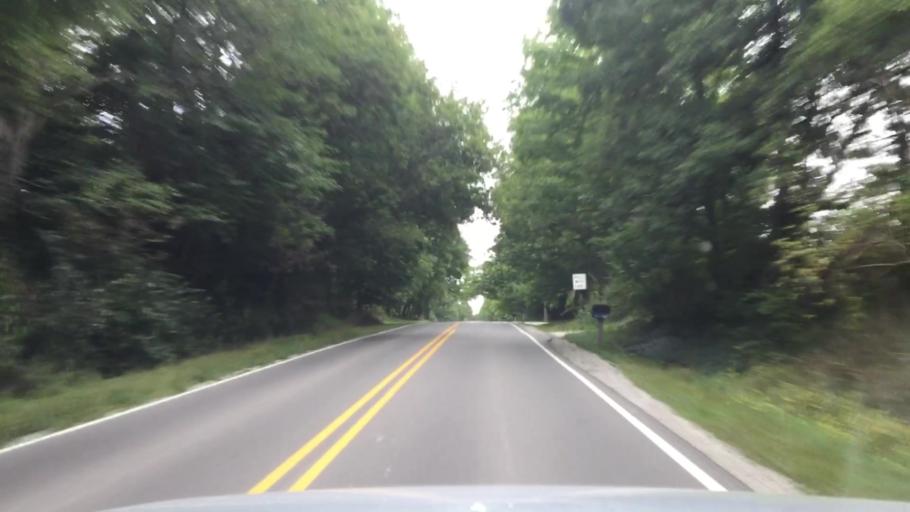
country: US
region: Michigan
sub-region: Washtenaw County
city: Ypsilanti
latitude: 42.1811
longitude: -83.6391
